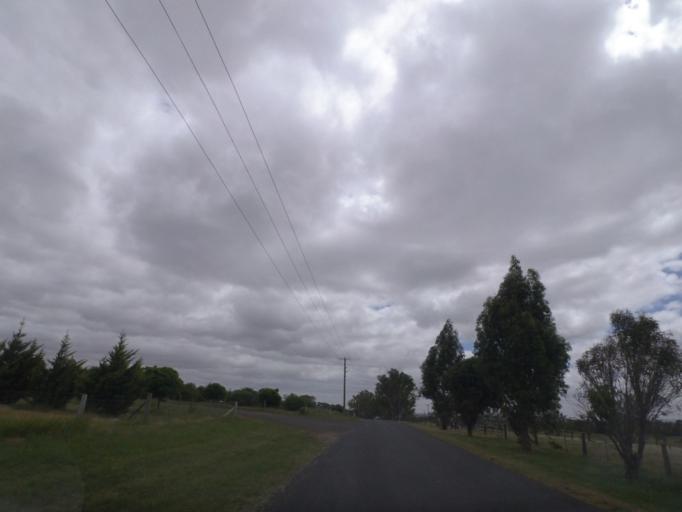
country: AU
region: Victoria
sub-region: Whittlesea
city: Whittlesea
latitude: -37.1834
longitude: 145.0380
